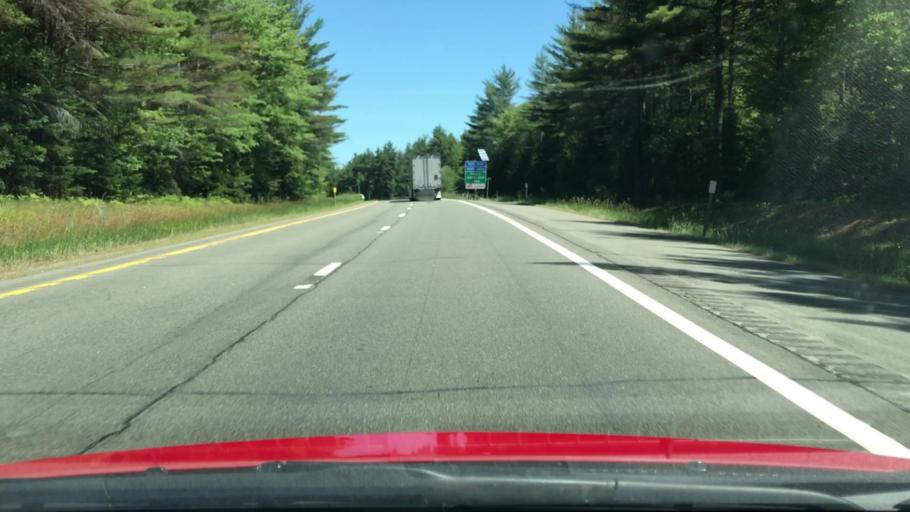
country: US
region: New York
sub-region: Essex County
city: Mineville
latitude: 43.9991
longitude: -73.7183
